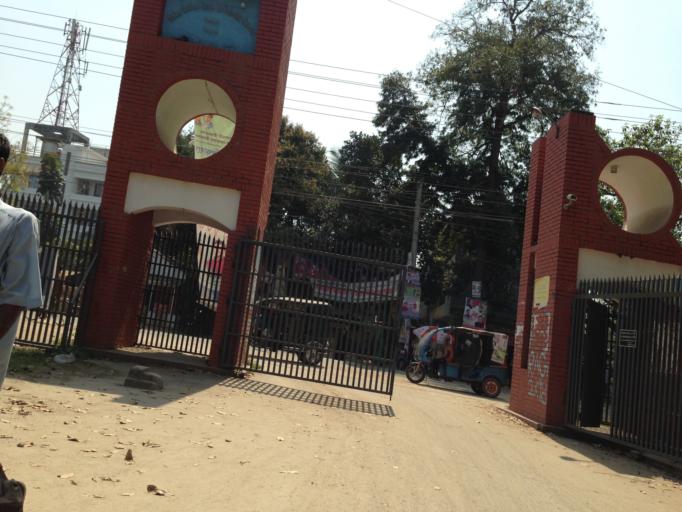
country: BD
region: Dhaka
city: Tangail
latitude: 24.2339
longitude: 89.8924
